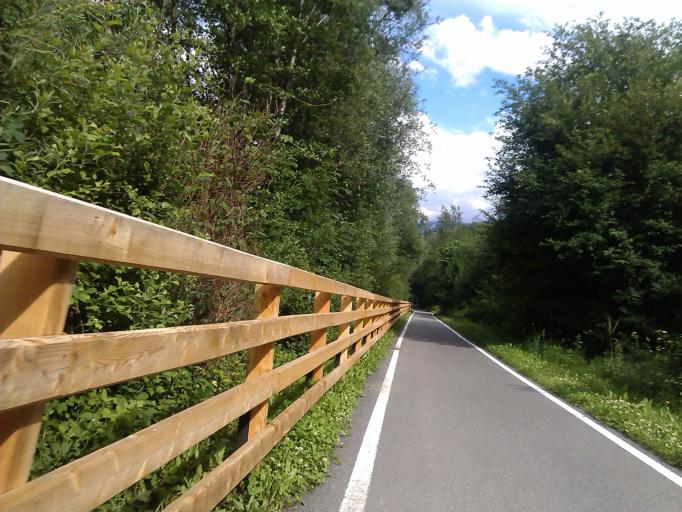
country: IT
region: Trentino-Alto Adige
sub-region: Bolzano
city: Sluderno
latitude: 46.6445
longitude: 10.5826
